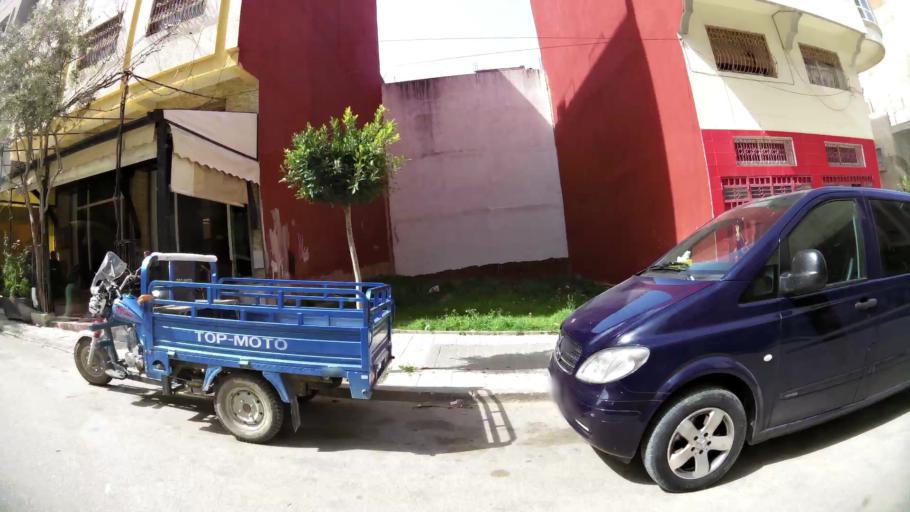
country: MA
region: Tanger-Tetouan
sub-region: Tanger-Assilah
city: Tangier
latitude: 35.7398
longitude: -5.8325
